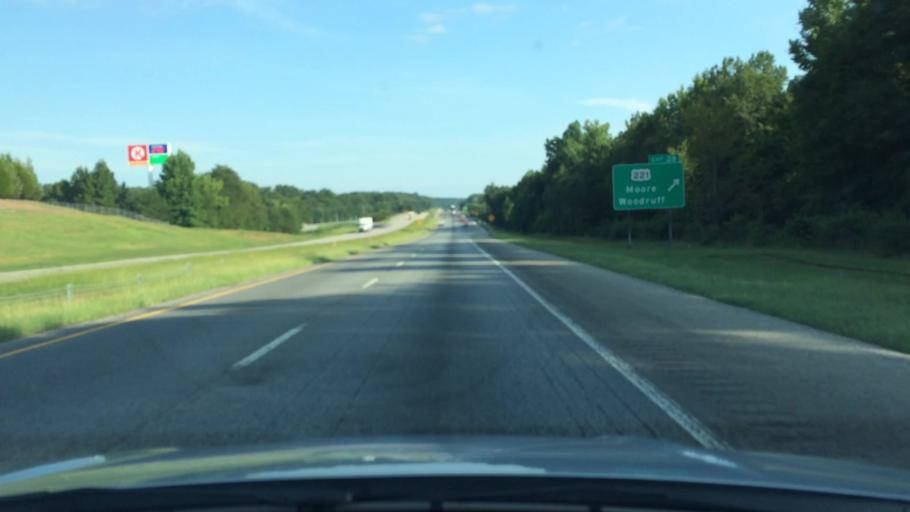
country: US
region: South Carolina
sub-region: Spartanburg County
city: Roebuck
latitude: 34.8429
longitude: -81.9729
